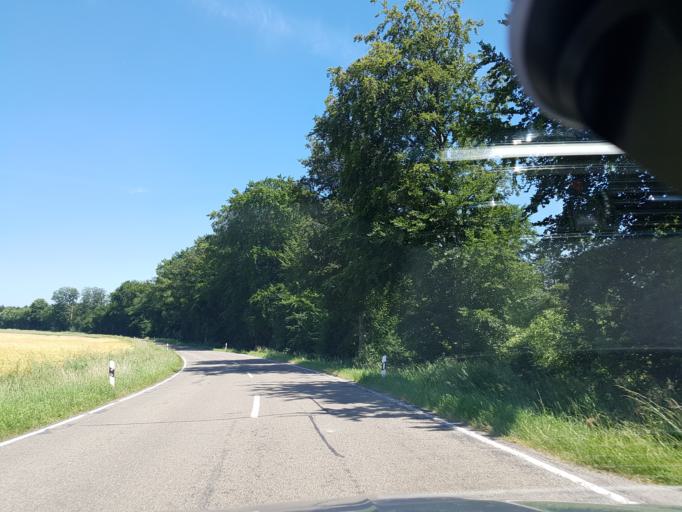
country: DE
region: Baden-Wuerttemberg
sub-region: Tuebingen Region
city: Blaubeuren
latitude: 48.4162
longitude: 9.8296
